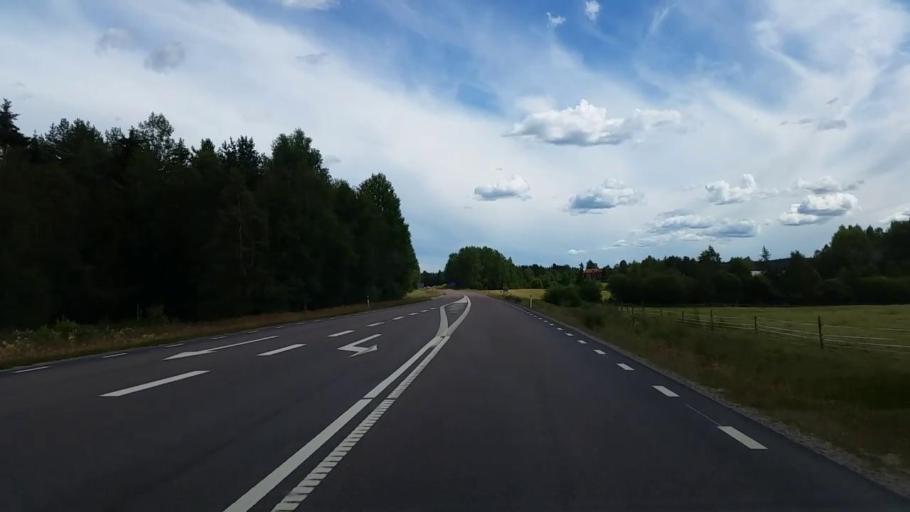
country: SE
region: Gaevleborg
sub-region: Ovanakers Kommun
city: Edsbyn
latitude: 61.3718
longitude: 15.8497
